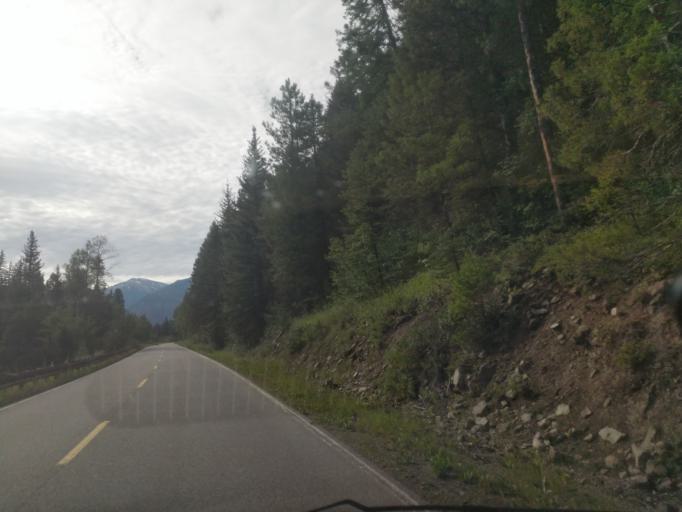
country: US
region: Colorado
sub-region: Garfield County
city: Carbondale
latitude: 39.0917
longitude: -107.2538
